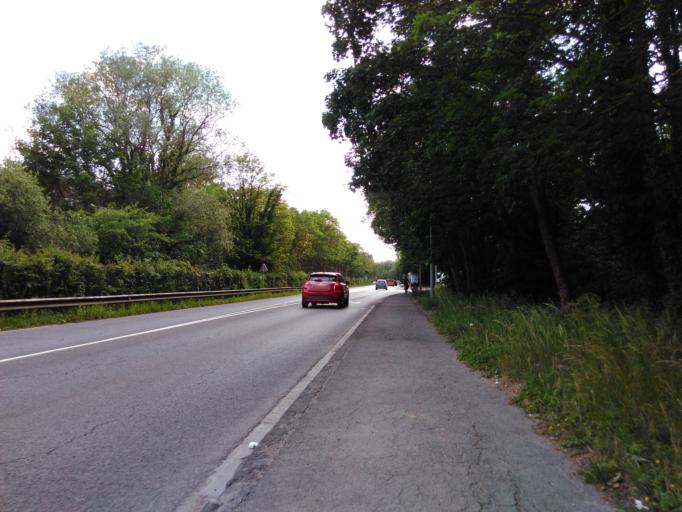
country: LU
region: Luxembourg
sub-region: Canton d'Esch-sur-Alzette
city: Schifflange
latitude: 49.5092
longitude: 5.9981
